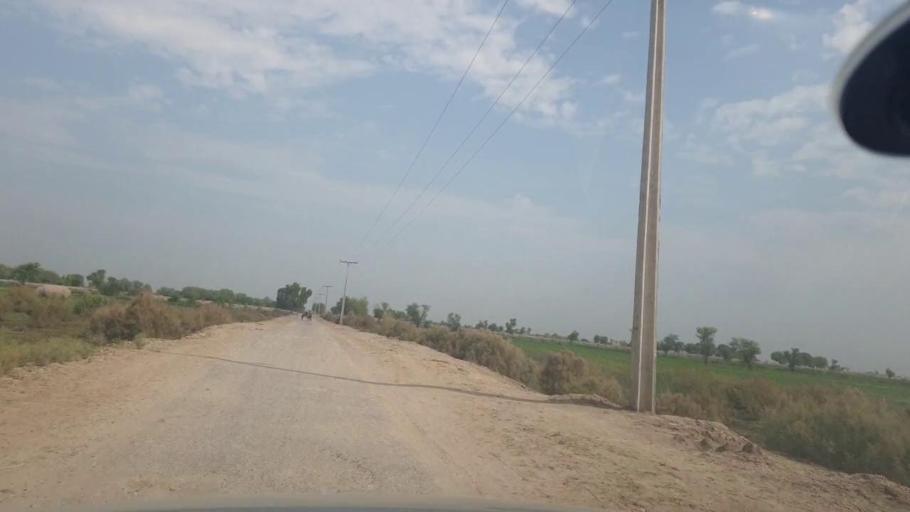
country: PK
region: Balochistan
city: Mehrabpur
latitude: 28.0590
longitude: 68.1055
